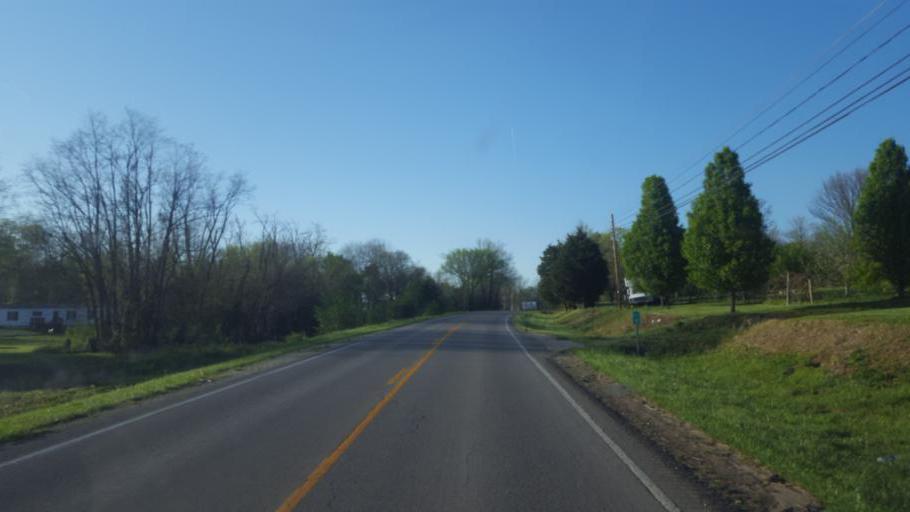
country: US
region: Kentucky
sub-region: Hart County
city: Munfordville
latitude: 37.2400
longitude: -85.8925
